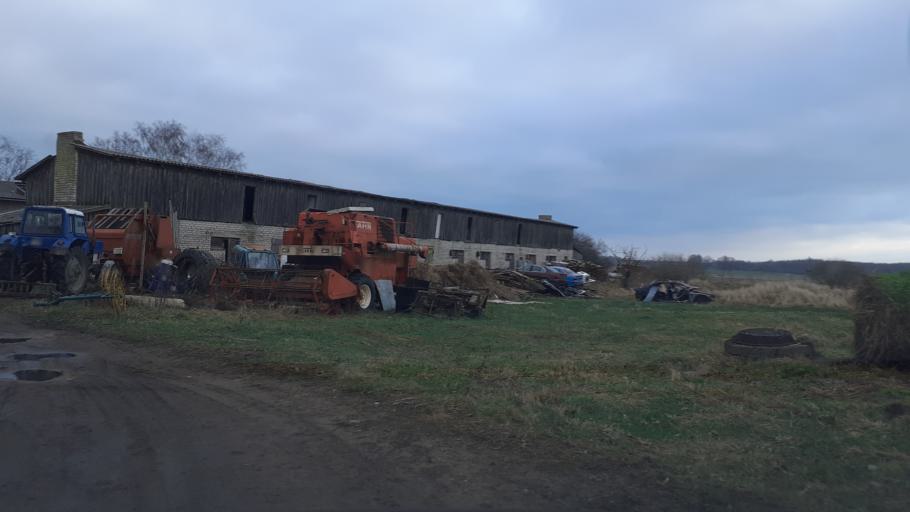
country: LV
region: Aizpute
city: Aizpute
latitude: 56.7996
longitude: 21.6705
